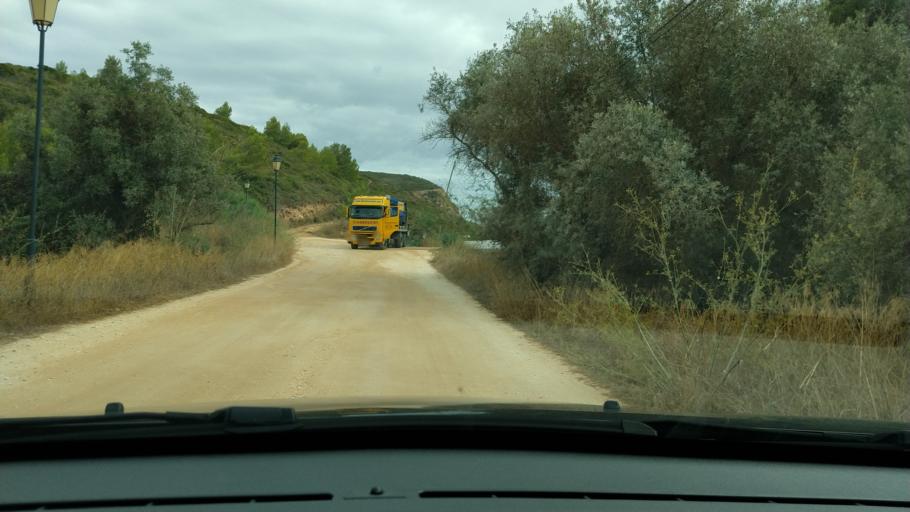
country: PT
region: Faro
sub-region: Vila do Bispo
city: Vila do Bispo
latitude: 37.0681
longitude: -8.7967
